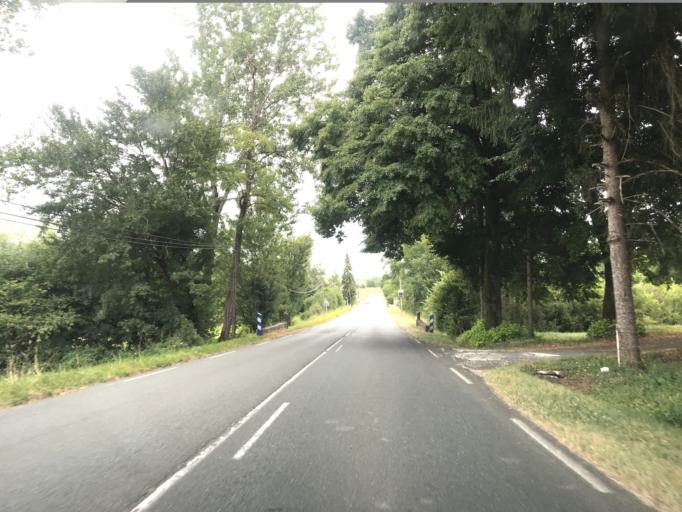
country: FR
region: Aquitaine
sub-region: Departement de la Dordogne
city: Brantome
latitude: 45.4071
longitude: 0.5842
